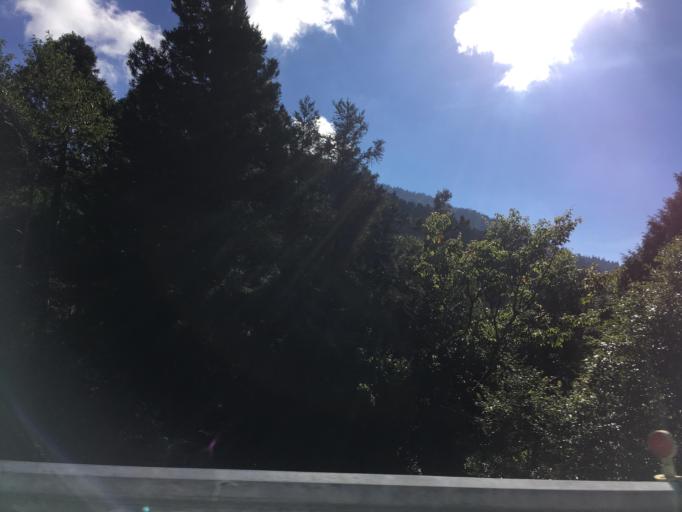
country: TW
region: Taiwan
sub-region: Yilan
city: Yilan
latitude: 24.5047
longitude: 121.5529
